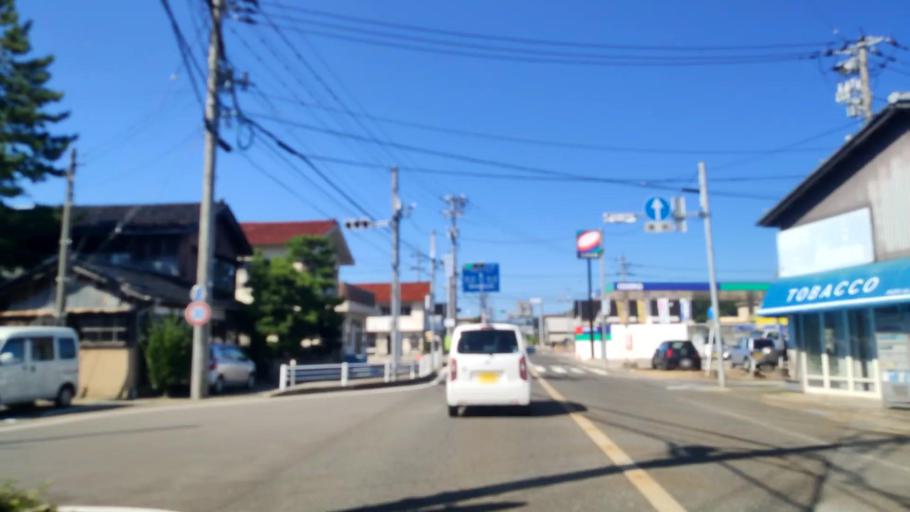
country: JP
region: Ishikawa
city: Nanao
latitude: 37.4430
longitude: 137.2646
